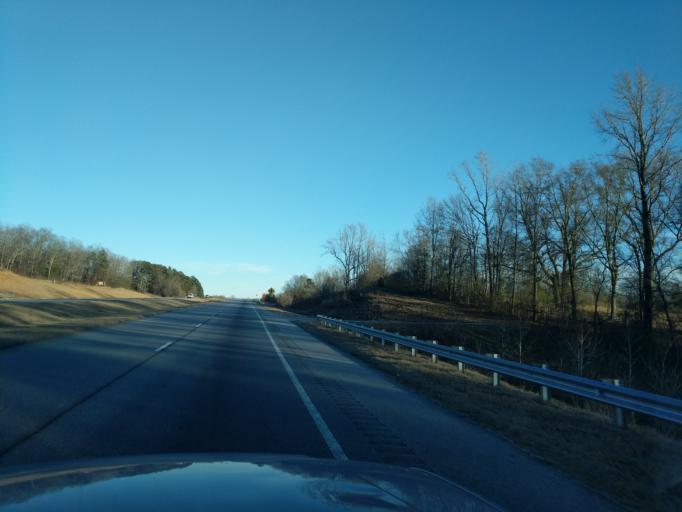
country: US
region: Georgia
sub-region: Stephens County
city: Toccoa
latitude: 34.5390
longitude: -83.3565
